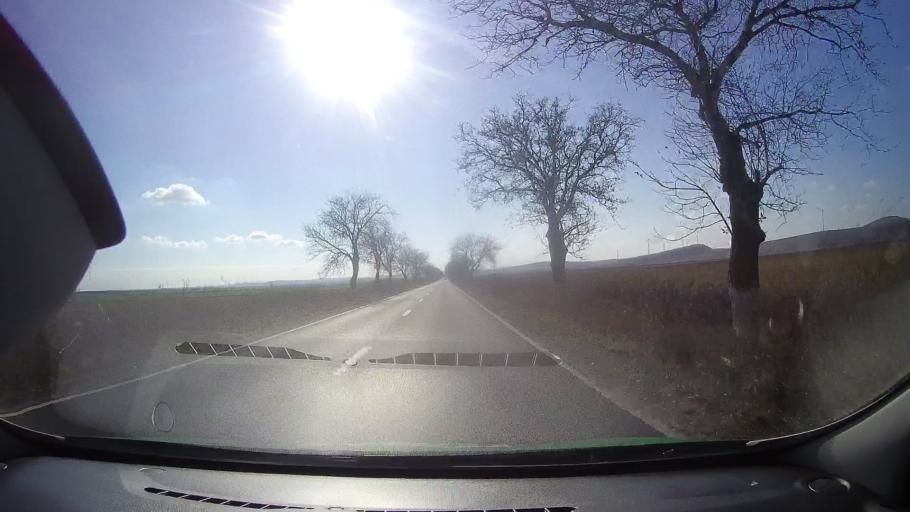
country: RO
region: Tulcea
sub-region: Comuna Ceamurlia de Jos
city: Ceamurlia de Jos
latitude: 44.7953
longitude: 28.6902
